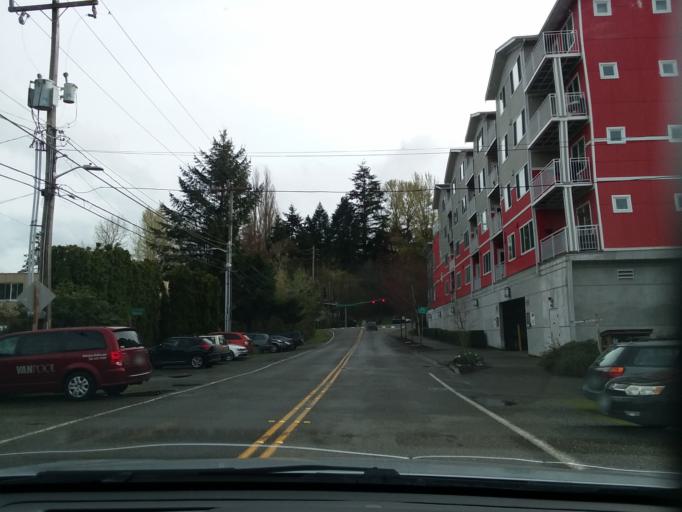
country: US
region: Washington
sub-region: Snohomish County
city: Mountlake Terrace
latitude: 47.7712
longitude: -122.3029
